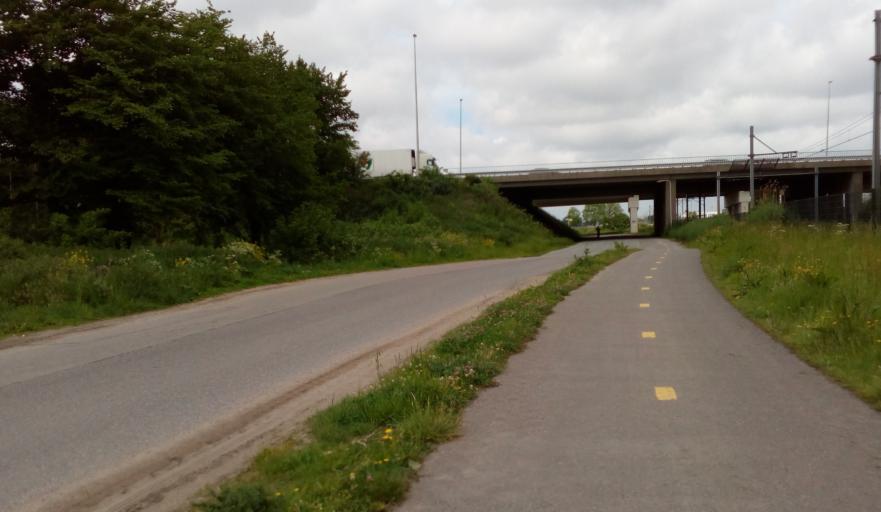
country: NL
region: South Holland
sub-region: Gemeente Waddinxveen
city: Waddinxveen
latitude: 52.0202
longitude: 4.6486
